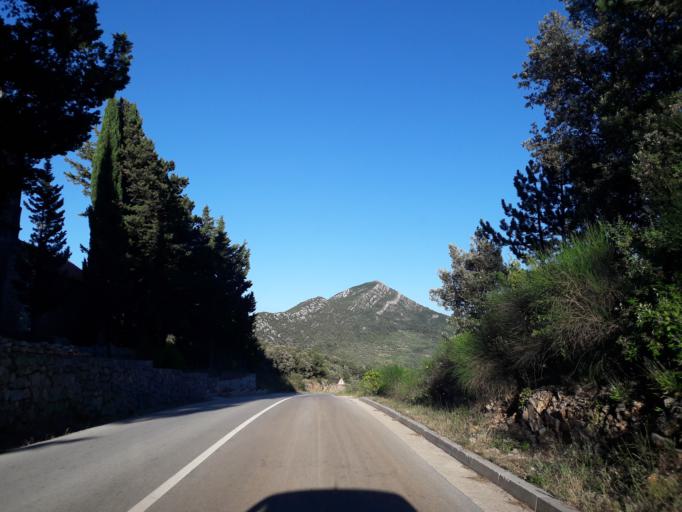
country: HR
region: Dubrovacko-Neretvanska
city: Orebic
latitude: 42.9987
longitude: 17.2594
